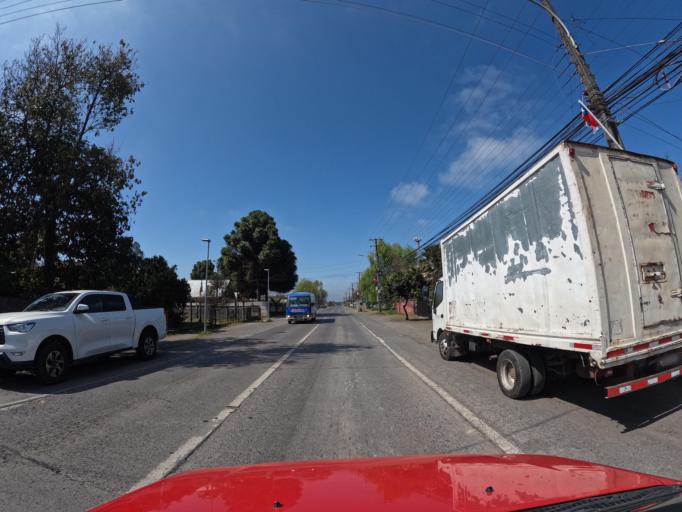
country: CL
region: Maule
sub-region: Provincia de Curico
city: Molina
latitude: -35.0592
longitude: -71.2656
